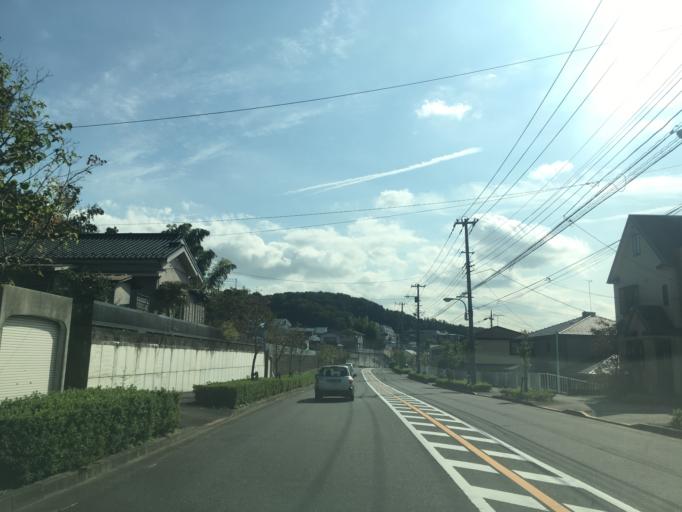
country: JP
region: Tokyo
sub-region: Machida-shi
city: Machida
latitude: 35.5918
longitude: 139.4164
